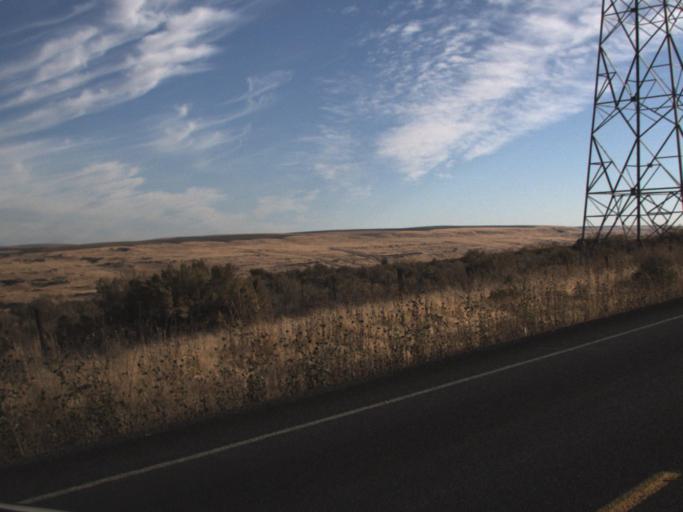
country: US
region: Washington
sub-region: Franklin County
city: Connell
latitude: 46.6299
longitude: -118.7323
